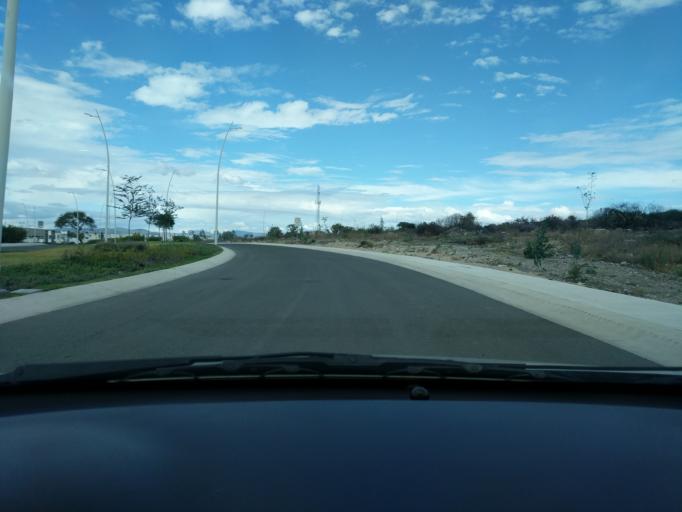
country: MX
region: Queretaro
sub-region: El Marques
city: El Pozo
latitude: 20.6455
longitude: -100.3123
